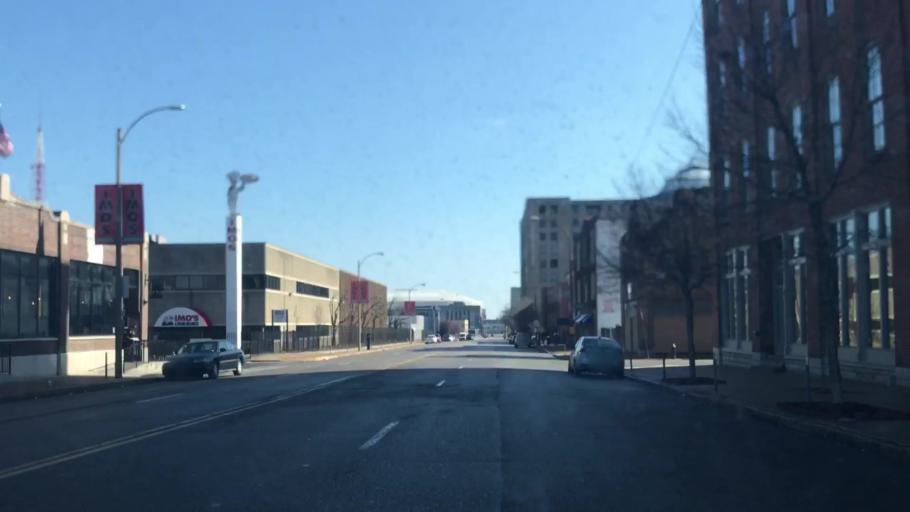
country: US
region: Missouri
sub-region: City of Saint Louis
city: St. Louis
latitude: 38.6347
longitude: -90.2033
